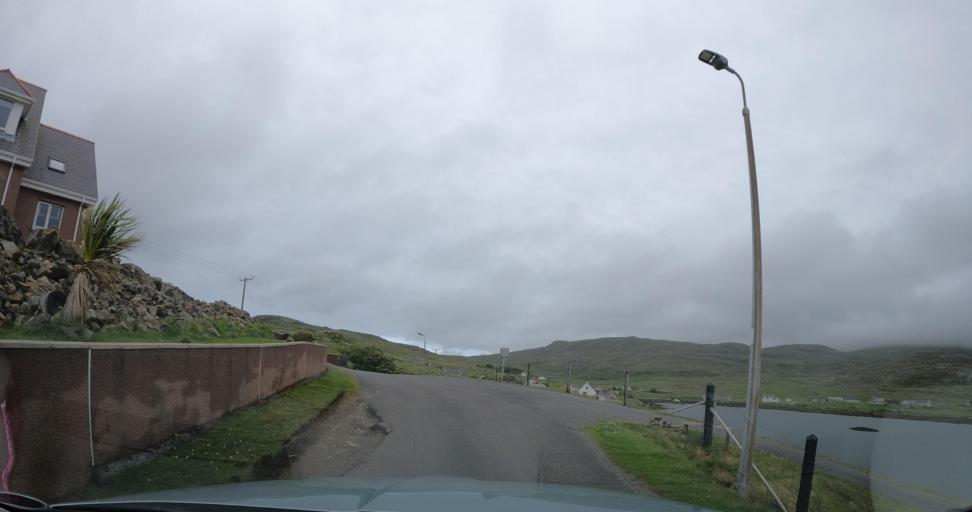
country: GB
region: Scotland
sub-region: Eilean Siar
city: Barra
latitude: 56.9542
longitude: -7.5071
